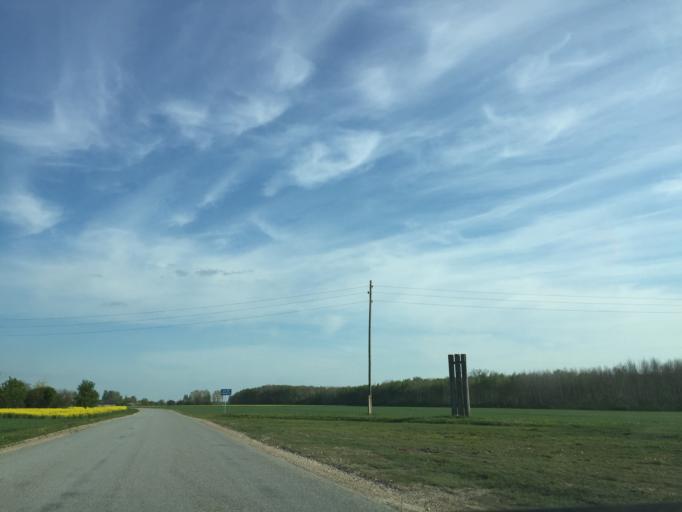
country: LV
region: Bauskas Rajons
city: Bauska
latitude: 56.3839
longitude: 24.2086
